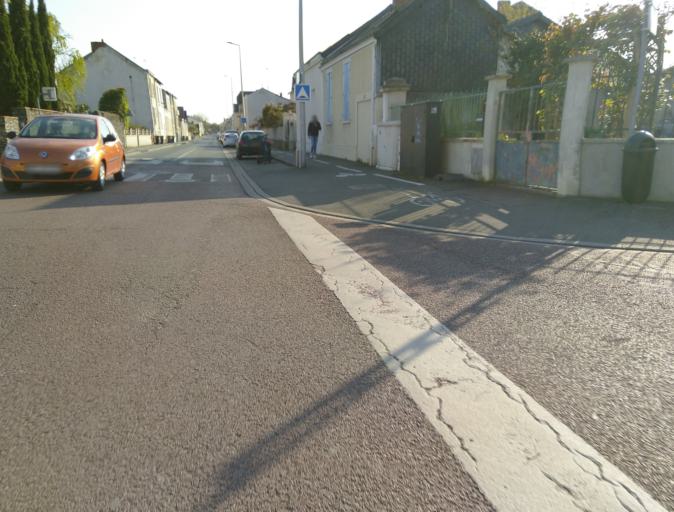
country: FR
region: Pays de la Loire
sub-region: Departement de Maine-et-Loire
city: Angers
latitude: 47.4563
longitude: -0.5239
